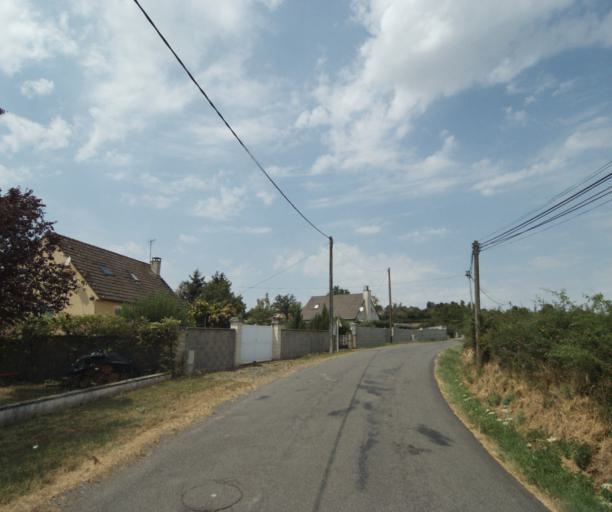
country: FR
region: Bourgogne
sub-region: Departement de Saone-et-Loire
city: Gueugnon
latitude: 46.5963
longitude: 4.0273
